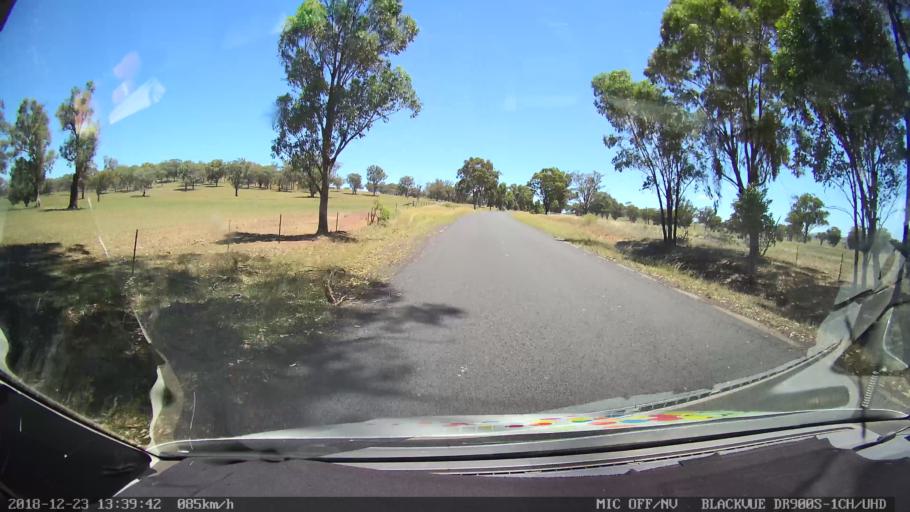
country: AU
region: New South Wales
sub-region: Armidale Dumaresq
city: Armidale
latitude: -30.4606
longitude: 151.1987
